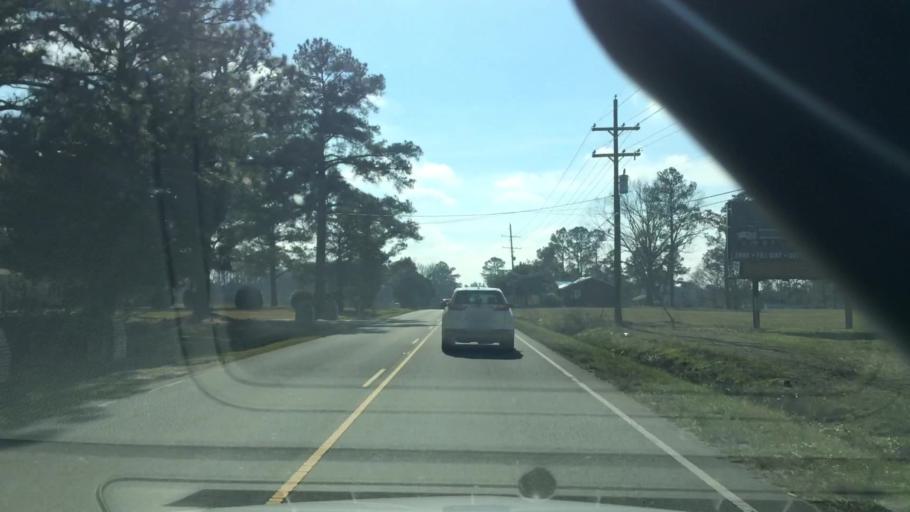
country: US
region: North Carolina
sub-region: Duplin County
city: Beulaville
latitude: 34.8947
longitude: -77.7822
